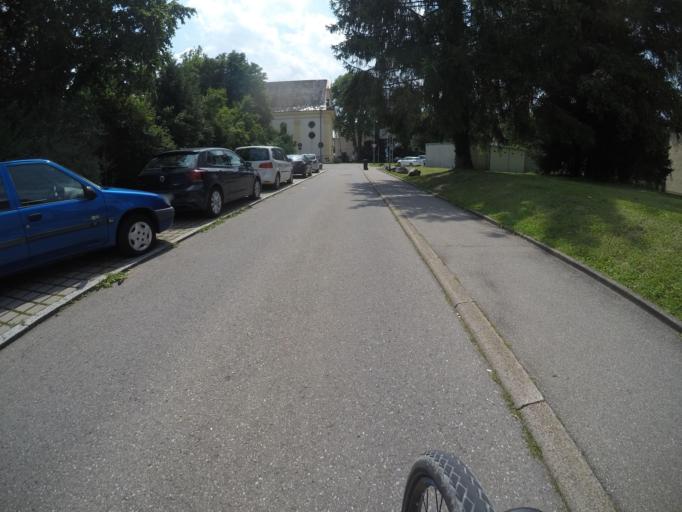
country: DE
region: Baden-Wuerttemberg
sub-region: Freiburg Region
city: Rottweil
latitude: 48.1627
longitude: 8.6362
